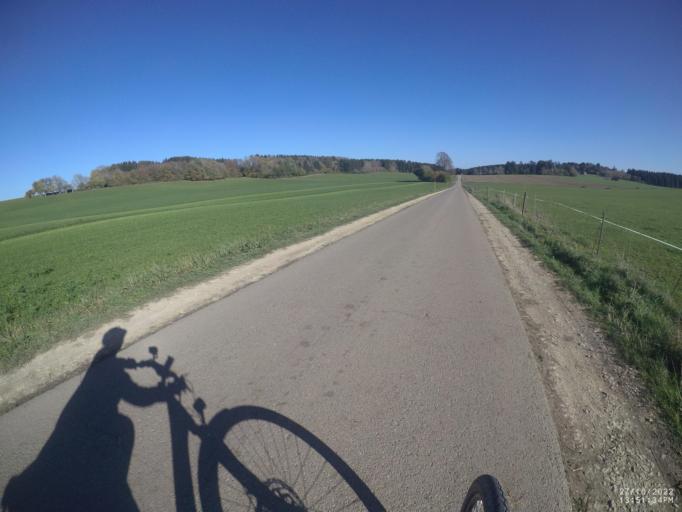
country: DE
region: Baden-Wuerttemberg
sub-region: Regierungsbezirk Stuttgart
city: Bad Ditzenbach
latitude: 48.5614
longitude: 9.7075
